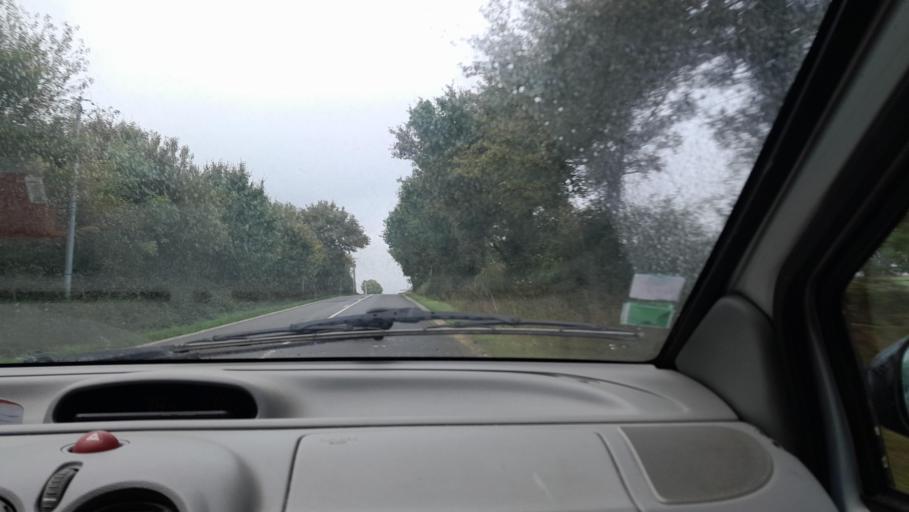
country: FR
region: Pays de la Loire
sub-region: Departement de la Mayenne
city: Congrier
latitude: 47.8227
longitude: -1.1445
